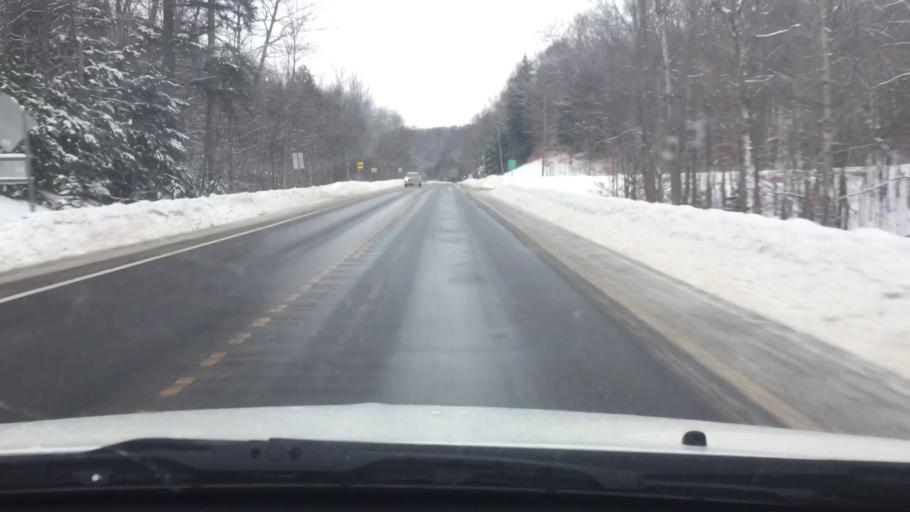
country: US
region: Michigan
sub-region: Charlevoix County
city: East Jordan
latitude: 45.1175
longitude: -85.0611
